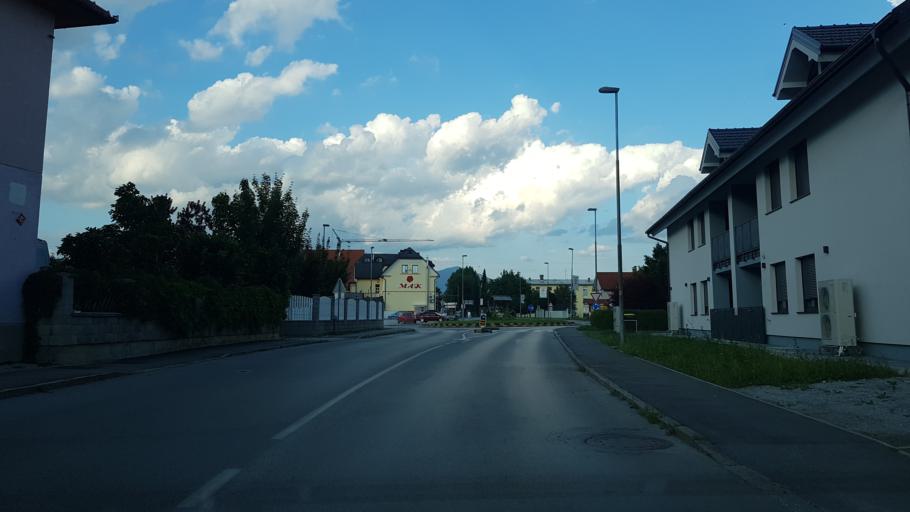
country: SI
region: Kranj
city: Zgornje Bitnje
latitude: 46.2308
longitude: 14.3443
